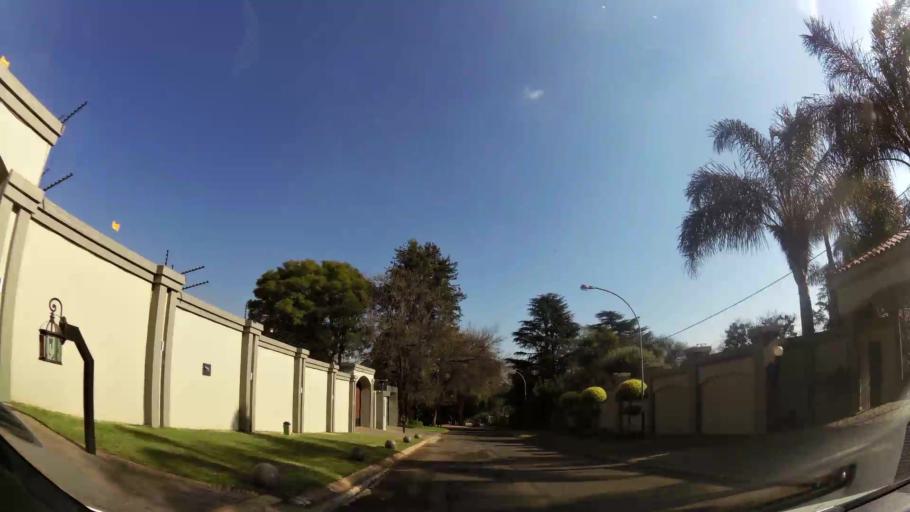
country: ZA
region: Gauteng
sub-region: Ekurhuleni Metropolitan Municipality
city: Germiston
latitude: -26.1782
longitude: 28.1459
